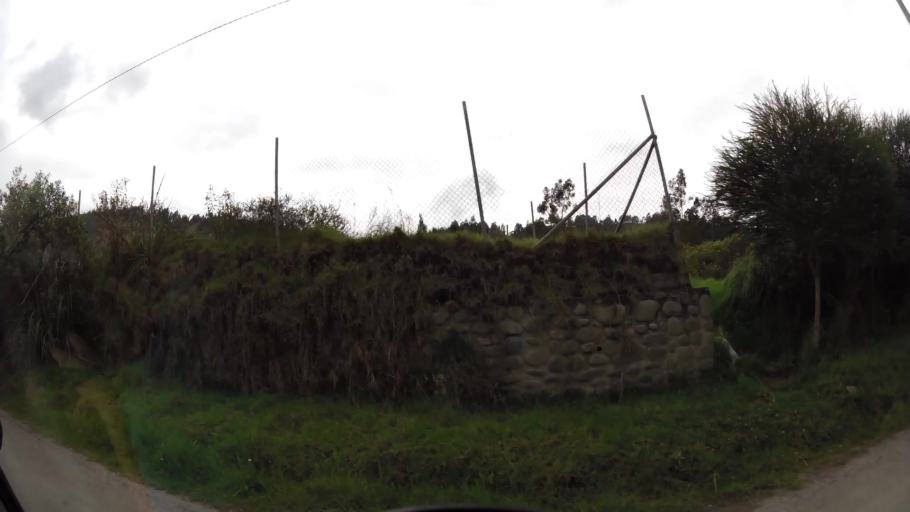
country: EC
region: Azuay
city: Cuenca
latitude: -2.8937
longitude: -78.9647
